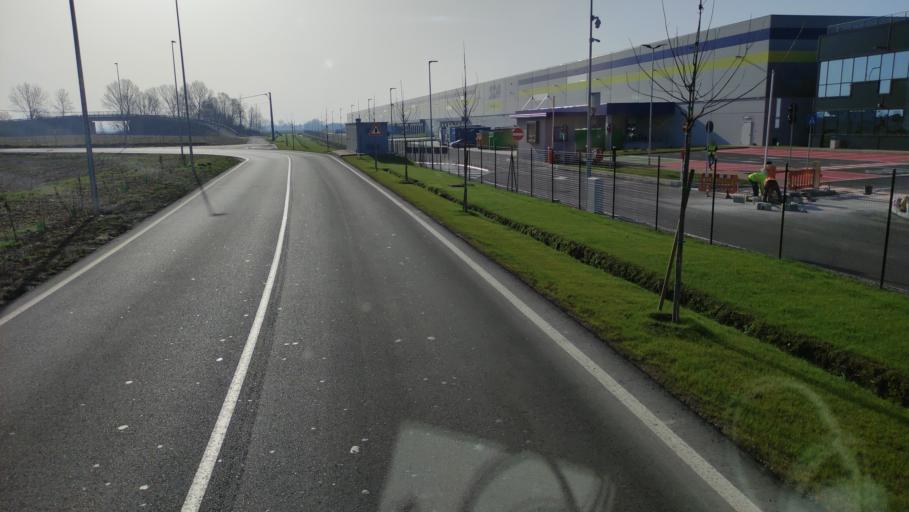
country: IT
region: Lombardy
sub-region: Provincia di Pavia
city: Landriano
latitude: 45.3036
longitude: 9.2726
